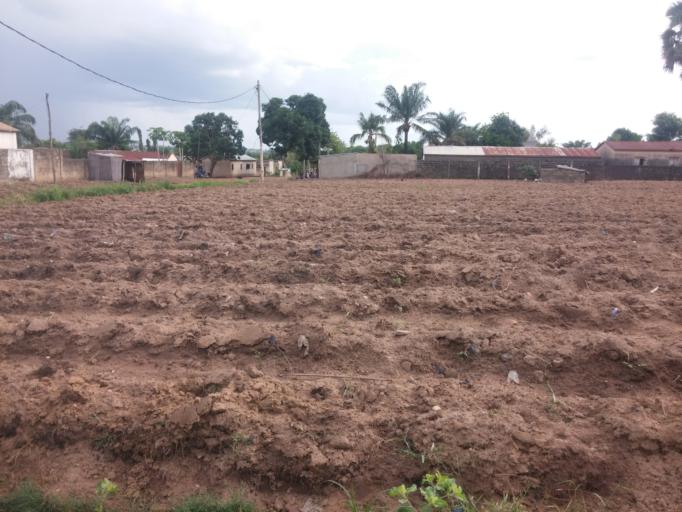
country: TG
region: Kara
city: Kara
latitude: 9.5472
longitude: 1.2054
